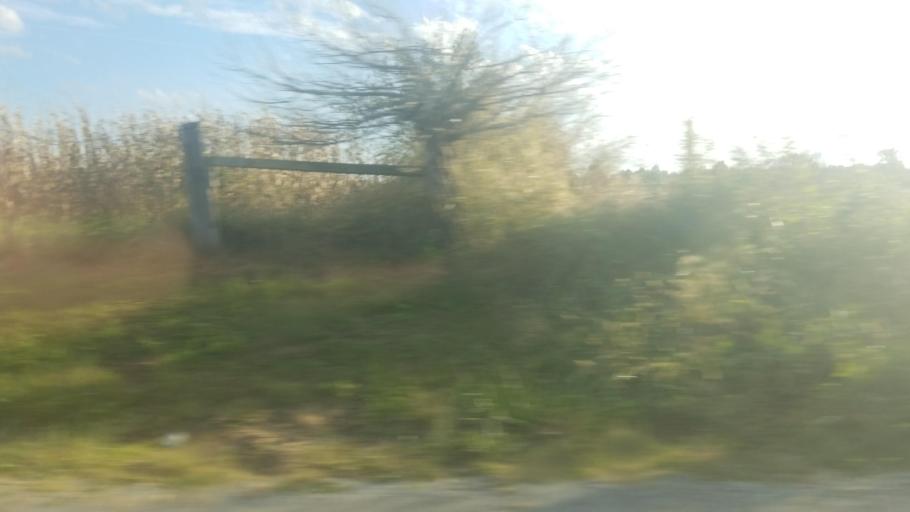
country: US
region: Illinois
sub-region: Saline County
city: Carrier Mills
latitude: 37.8050
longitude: -88.6793
